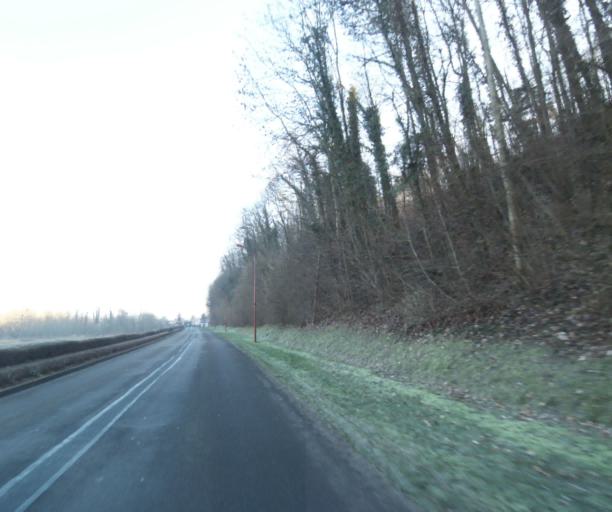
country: FR
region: Champagne-Ardenne
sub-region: Departement de la Haute-Marne
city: Bienville
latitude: 48.5475
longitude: 5.0749
